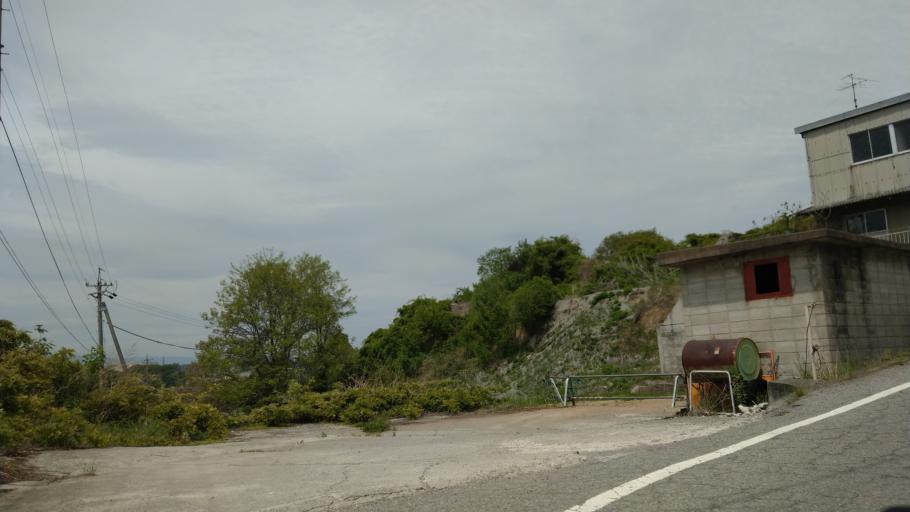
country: JP
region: Nagano
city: Komoro
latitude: 36.3142
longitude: 138.4627
